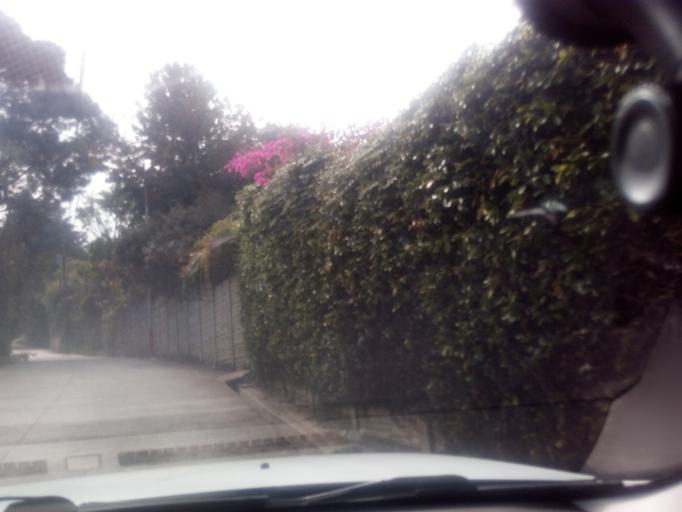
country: GT
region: Sacatepequez
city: San Bartolome Milpas Altas
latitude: 14.6011
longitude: -90.6783
